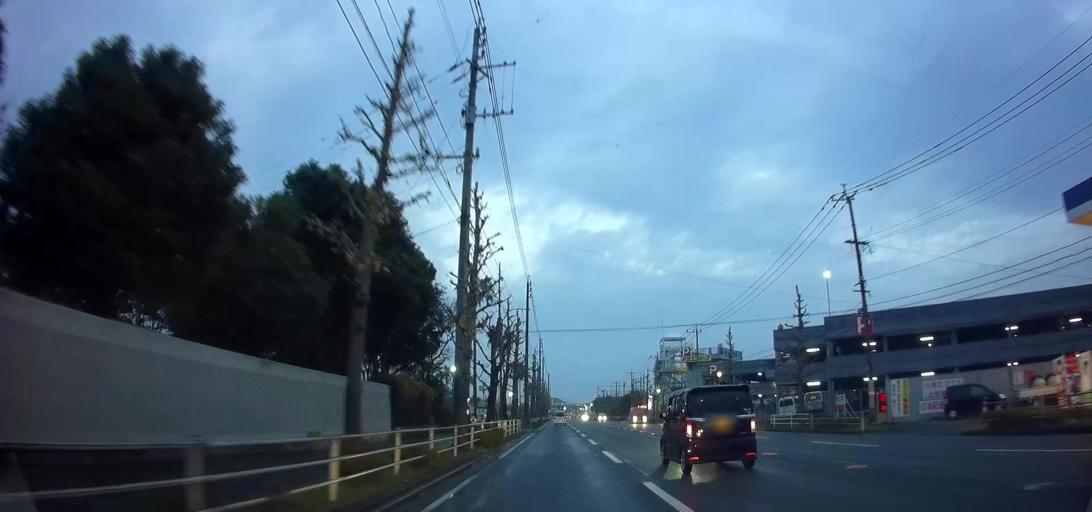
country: JP
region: Nagasaki
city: Omura
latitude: 32.9188
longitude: 129.9411
